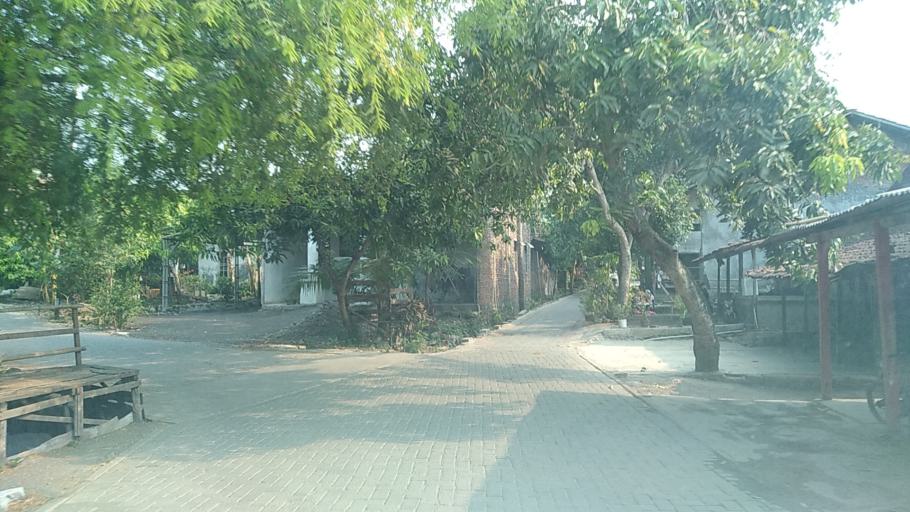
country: ID
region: Central Java
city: Mranggen
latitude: -7.0721
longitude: 110.4741
